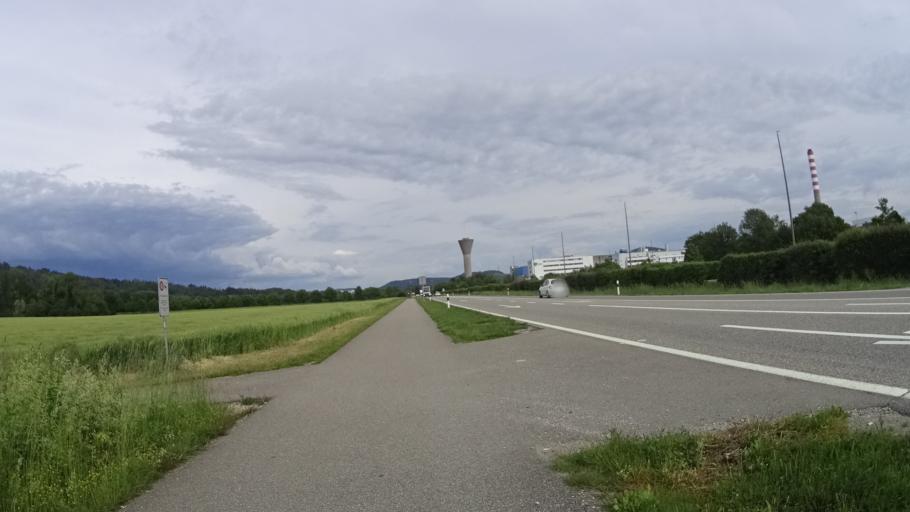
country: CH
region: Aargau
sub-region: Bezirk Laufenburg
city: Eiken
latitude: 47.5518
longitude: 7.9743
